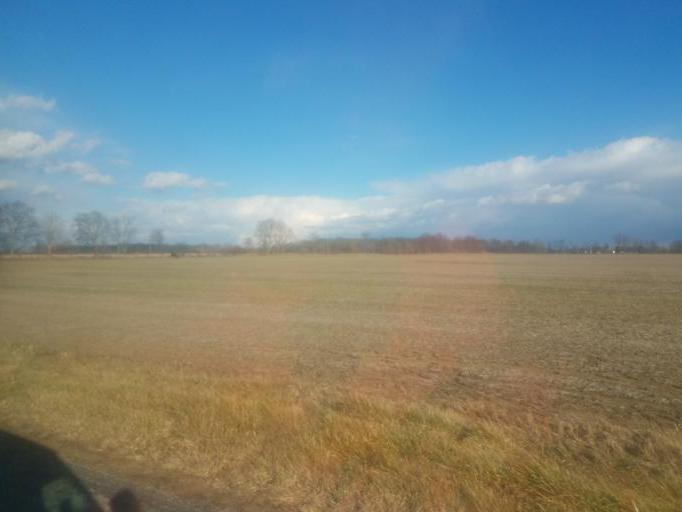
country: US
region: Ohio
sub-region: Marion County
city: Prospect
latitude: 40.3888
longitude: -83.1455
